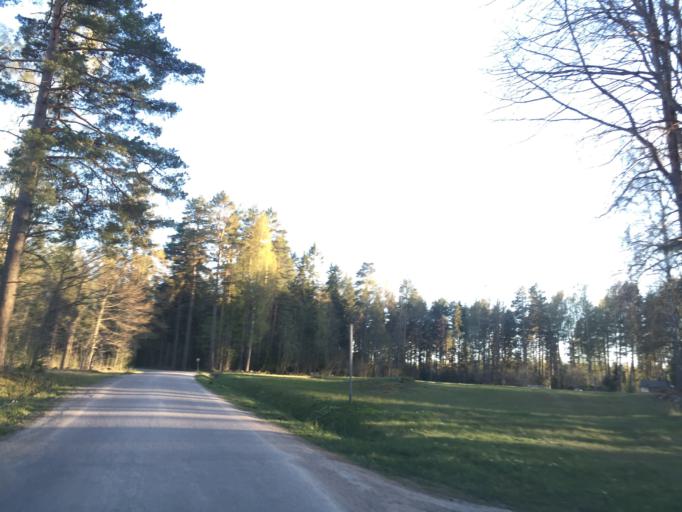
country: SE
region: OErebro
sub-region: Orebro Kommun
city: Odensbacken
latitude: 59.2356
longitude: 15.5646
